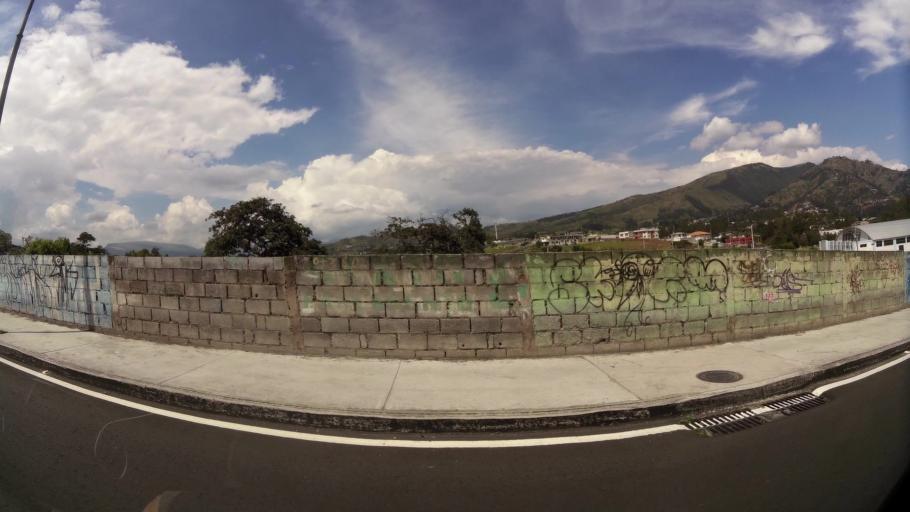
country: EC
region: Pichincha
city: Sangolqui
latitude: -0.2150
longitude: -78.3917
